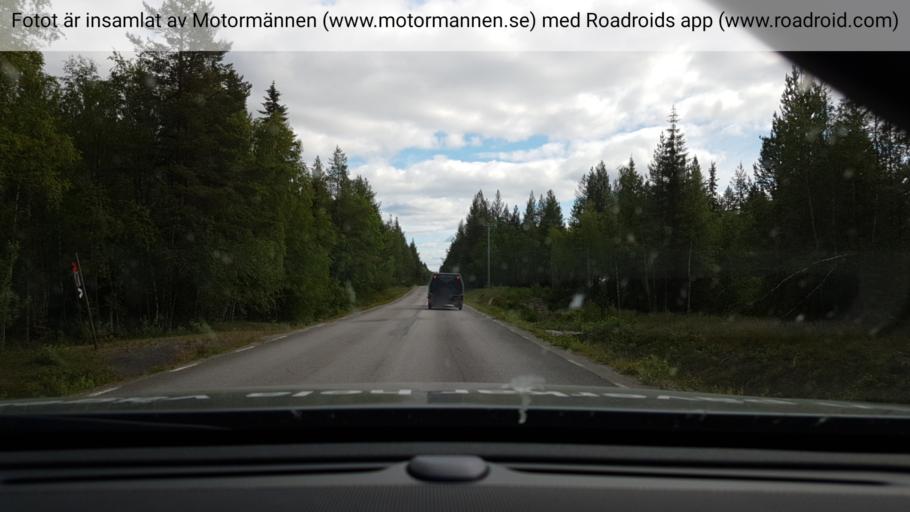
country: SE
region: Vaesterbotten
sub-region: Sorsele Kommun
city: Sorsele
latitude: 65.5522
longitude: 17.5276
